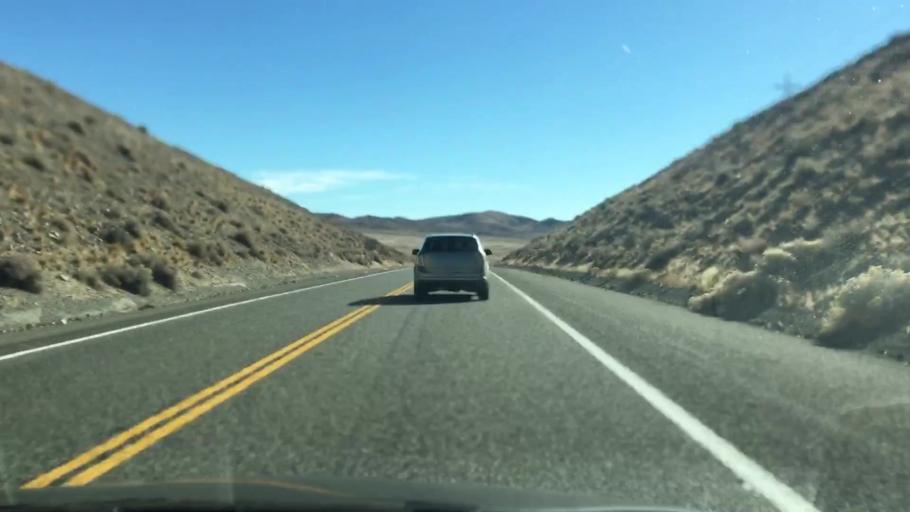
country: US
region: Nevada
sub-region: Lyon County
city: Silver Springs
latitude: 39.2133
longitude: -119.2193
